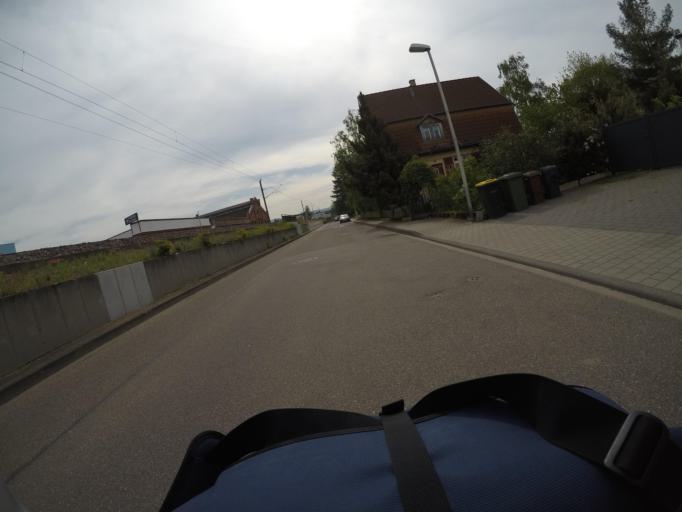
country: DE
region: Baden-Wuerttemberg
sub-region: Karlsruhe Region
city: Rastatt
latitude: 48.8550
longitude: 8.2198
